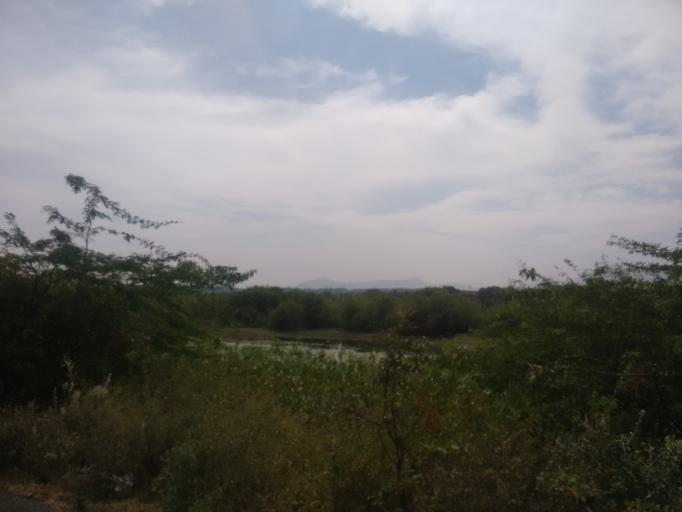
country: IN
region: Tamil Nadu
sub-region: Coimbatore
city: Perur
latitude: 10.9752
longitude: 76.9226
